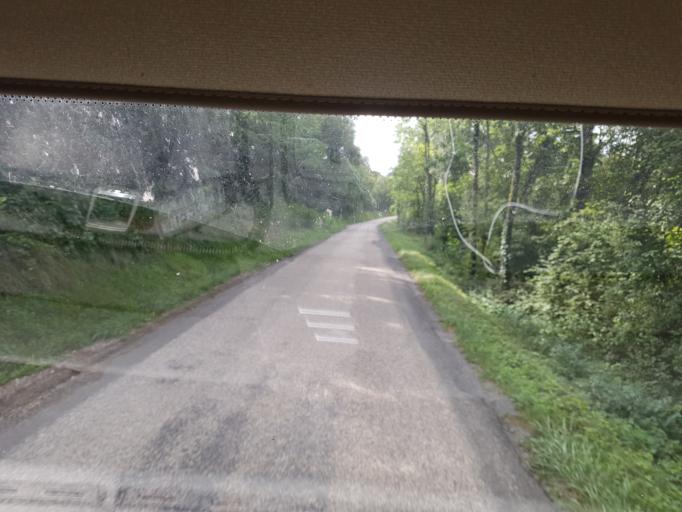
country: FR
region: Rhone-Alpes
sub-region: Departement de l'Ain
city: Poncin
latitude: 46.1170
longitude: 5.4003
